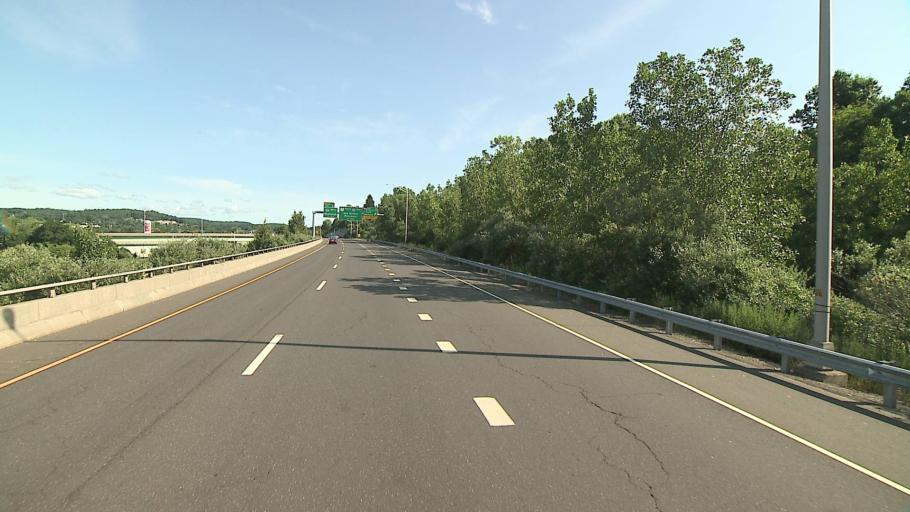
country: US
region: Connecticut
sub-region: Fairfield County
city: Danbury
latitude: 41.3752
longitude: -73.4731
